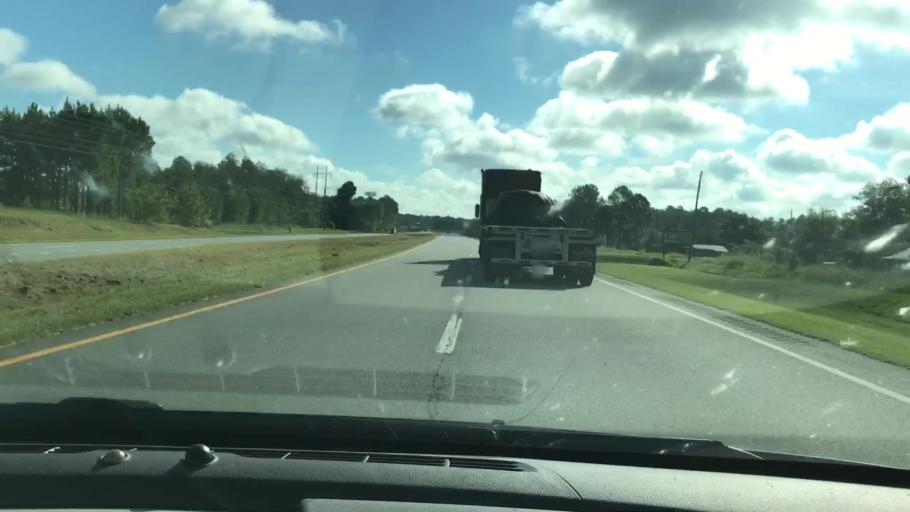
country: US
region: Georgia
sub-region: Worth County
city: Sylvester
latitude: 31.5506
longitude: -83.9614
